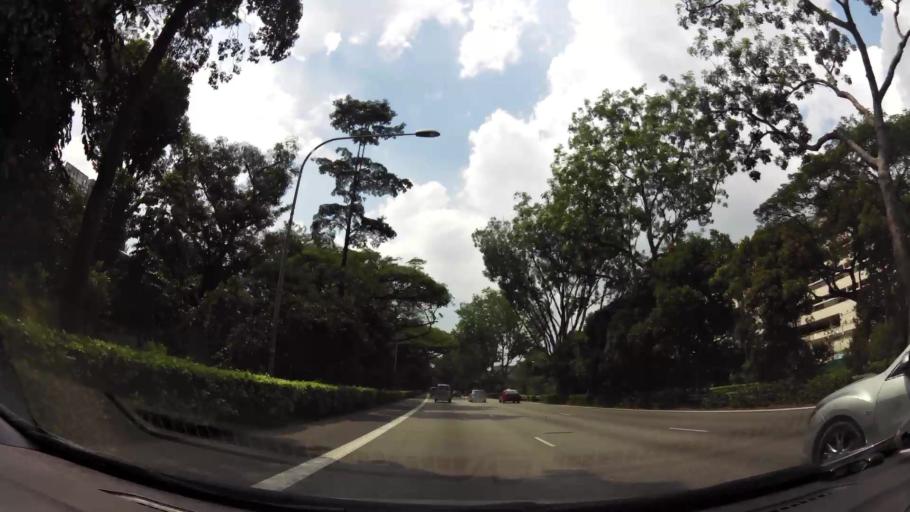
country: SG
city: Singapore
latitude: 1.2834
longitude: 103.8107
